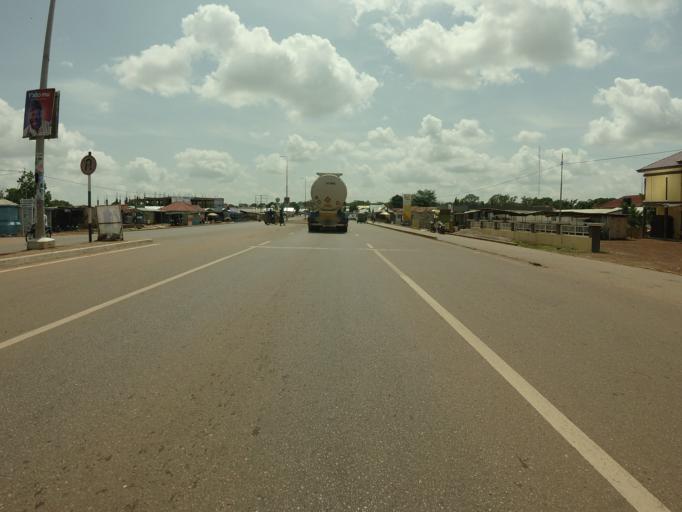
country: GH
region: Northern
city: Tamale
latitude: 9.3970
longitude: -0.8276
